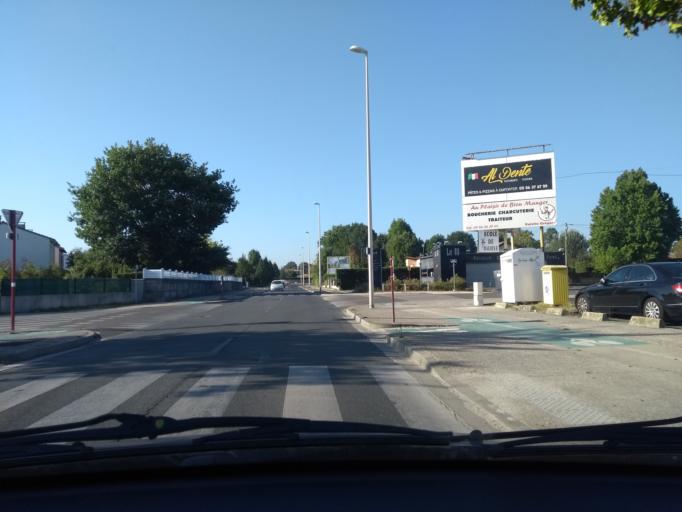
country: FR
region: Aquitaine
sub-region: Departement de la Gironde
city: Pessac
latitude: 44.7910
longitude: -0.6729
